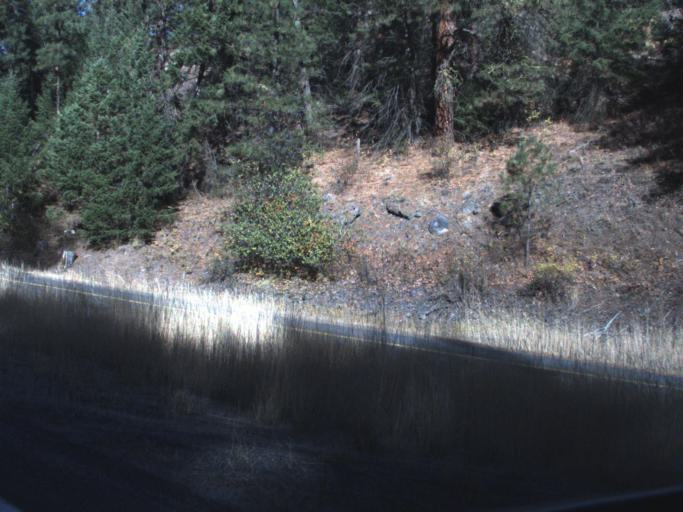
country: US
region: Washington
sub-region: Lincoln County
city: Davenport
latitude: 48.0513
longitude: -118.2216
